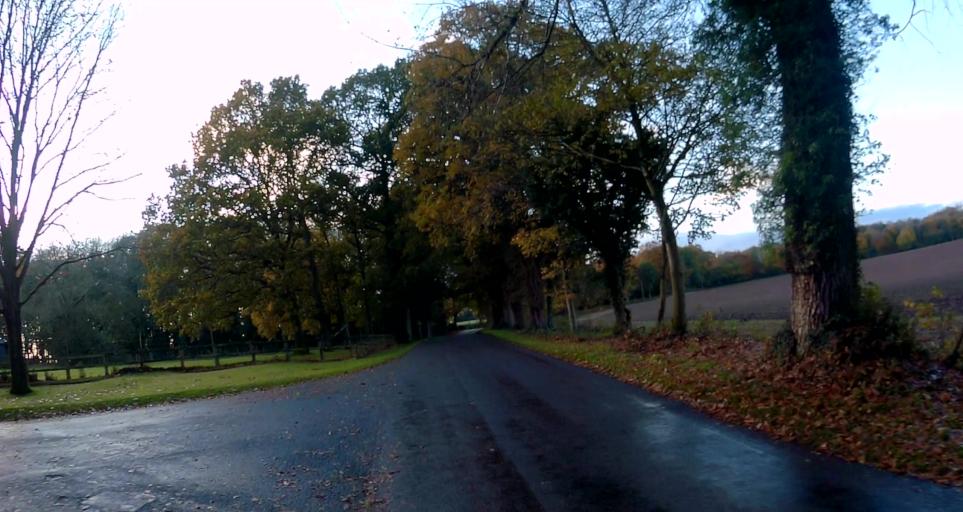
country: GB
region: England
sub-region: Hampshire
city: Basingstoke
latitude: 51.2173
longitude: -1.1132
